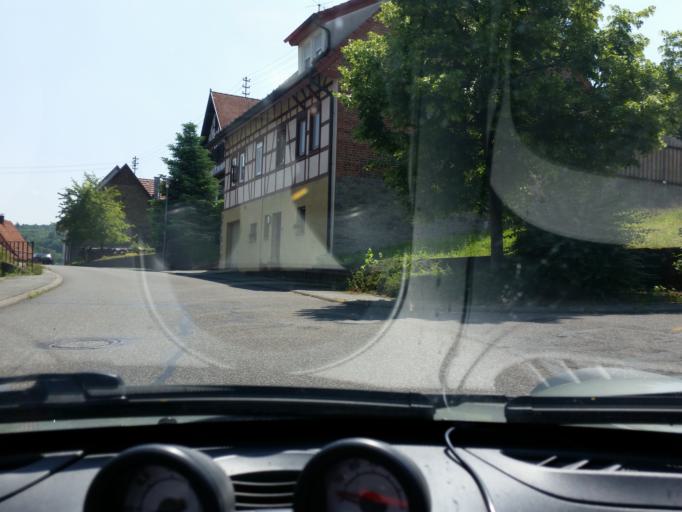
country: DE
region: Baden-Wuerttemberg
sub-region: Karlsruhe Region
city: Seckach
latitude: 49.4412
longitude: 9.3346
